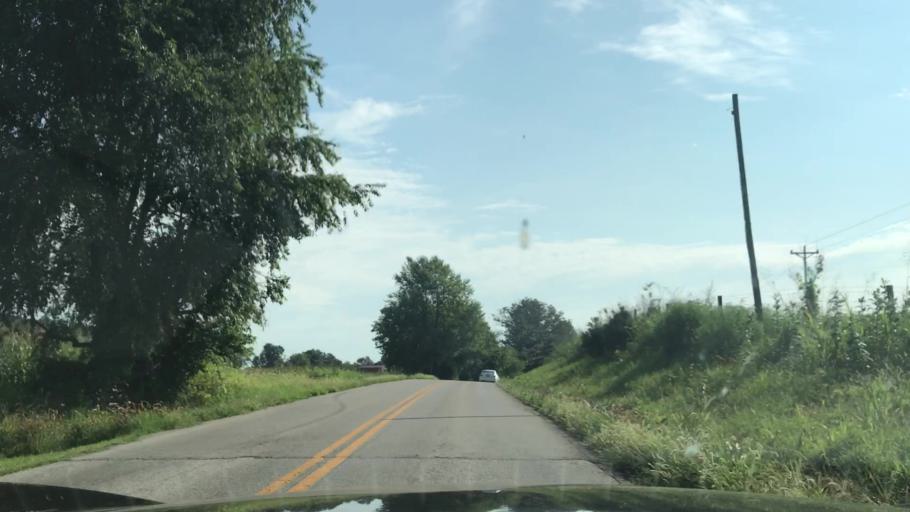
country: US
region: Kentucky
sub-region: Hart County
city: Munfordville
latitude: 37.2061
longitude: -85.7432
